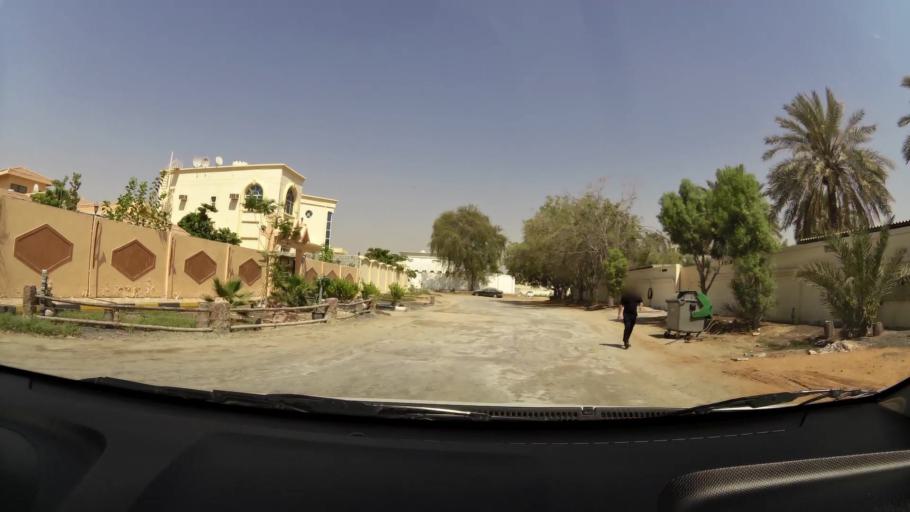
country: AE
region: Ajman
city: Ajman
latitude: 25.4145
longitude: 55.4753
